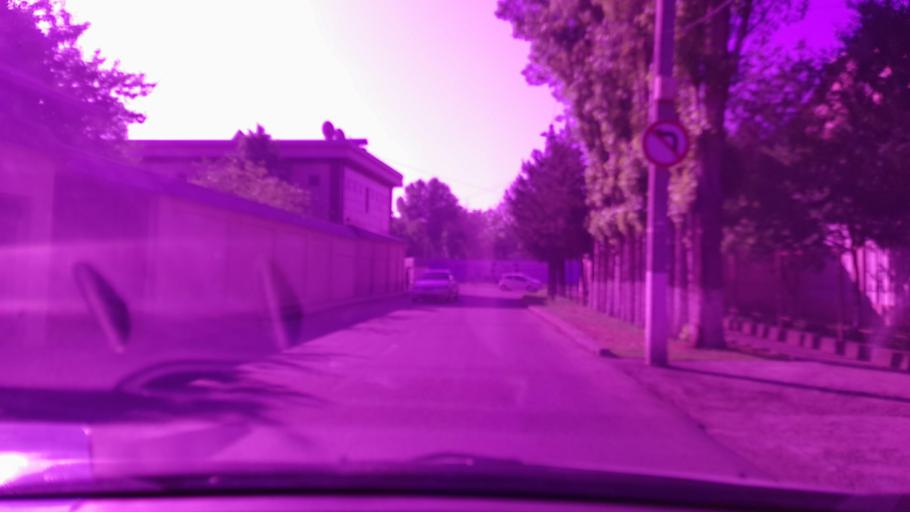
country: UZ
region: Toshkent
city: Salor
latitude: 41.3333
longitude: 69.3623
